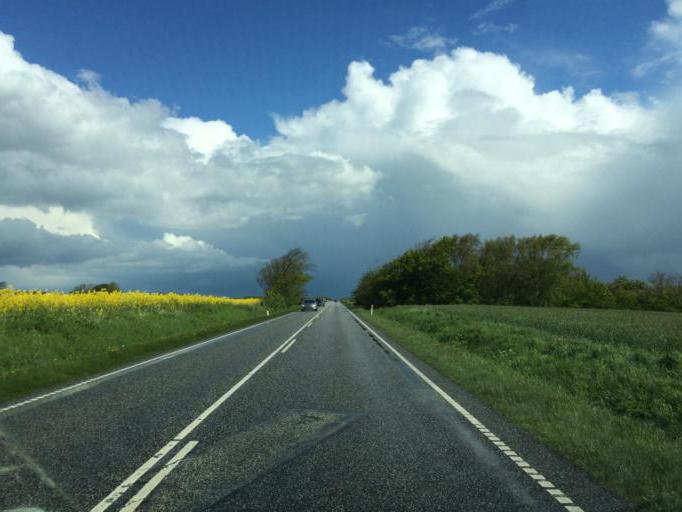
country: DK
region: Central Jutland
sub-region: Holstebro Kommune
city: Vinderup
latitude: 56.4279
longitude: 8.7107
